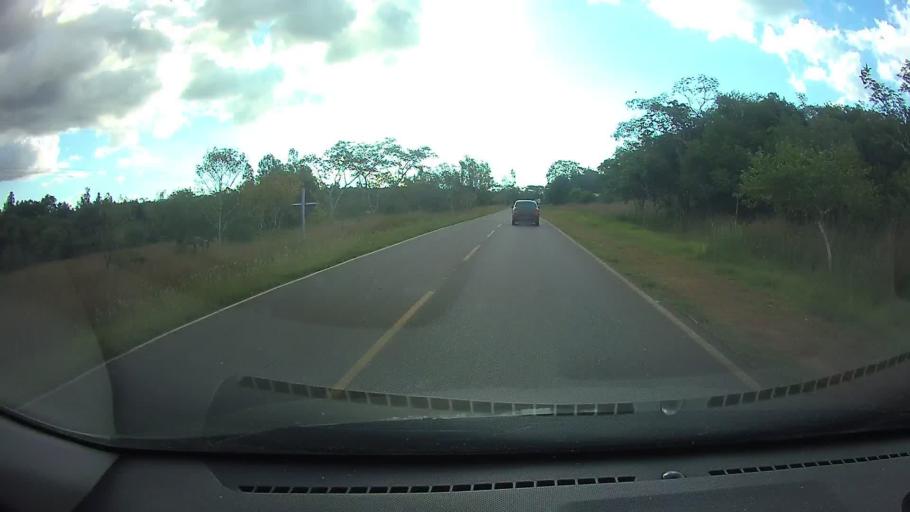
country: PY
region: Cordillera
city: Altos
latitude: -25.2829
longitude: -57.2081
